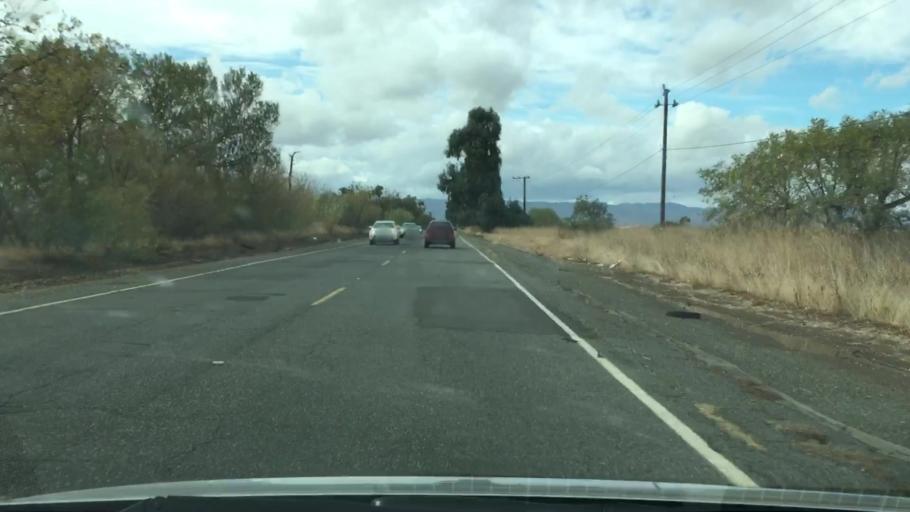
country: US
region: California
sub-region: Yolo County
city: Winters
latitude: 38.5616
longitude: -121.8781
